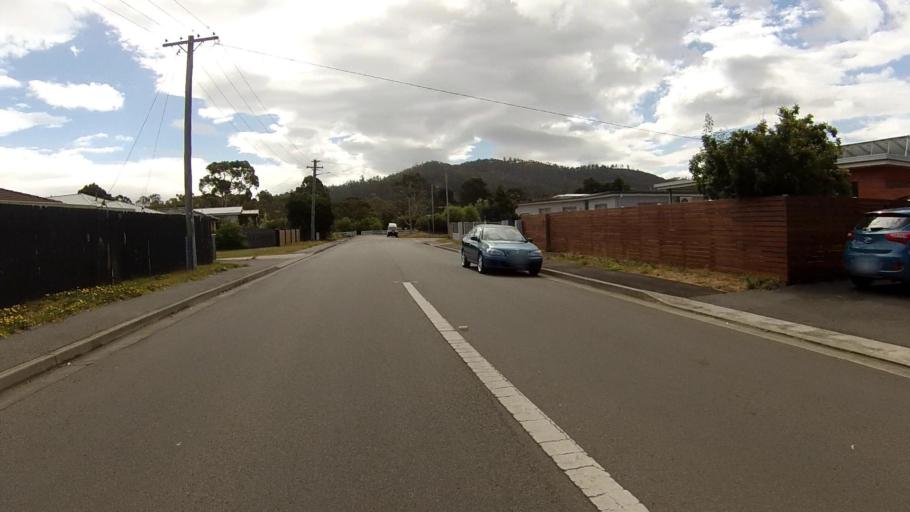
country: AU
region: Tasmania
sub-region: Clarence
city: Lauderdale
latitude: -42.9063
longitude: 147.4926
